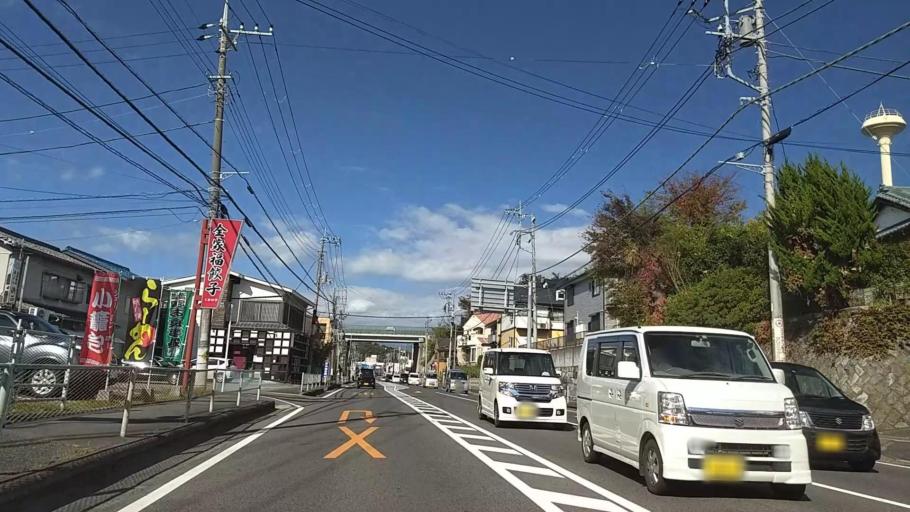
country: JP
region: Kanagawa
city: Ninomiya
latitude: 35.3098
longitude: 139.2470
